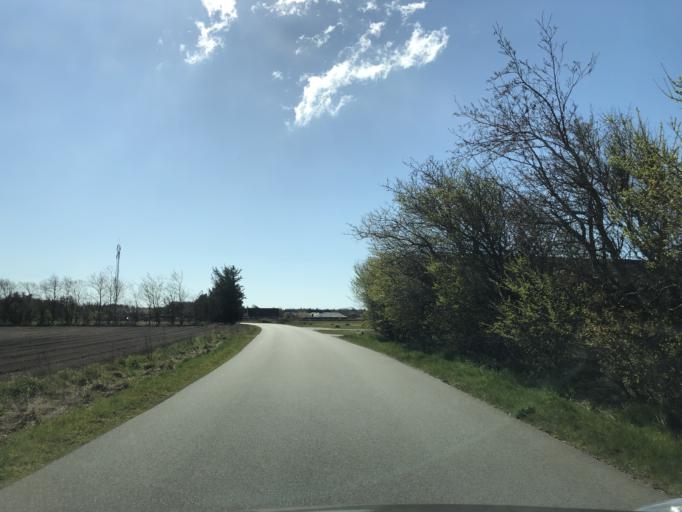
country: DK
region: Central Jutland
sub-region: Holstebro Kommune
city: Ulfborg
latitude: 56.3126
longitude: 8.1917
